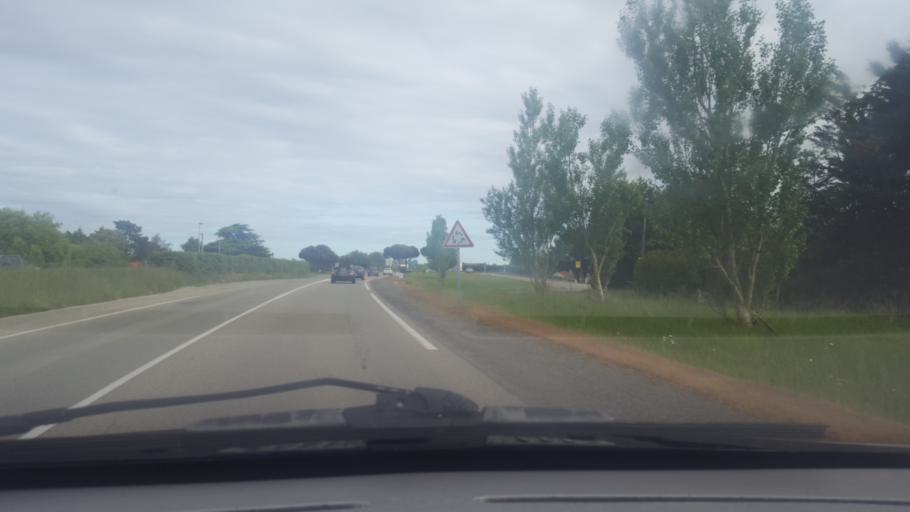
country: FR
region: Pays de la Loire
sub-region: Departement de la Loire-Atlantique
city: Bourgneuf-en-Retz
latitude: 47.0493
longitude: -1.9603
